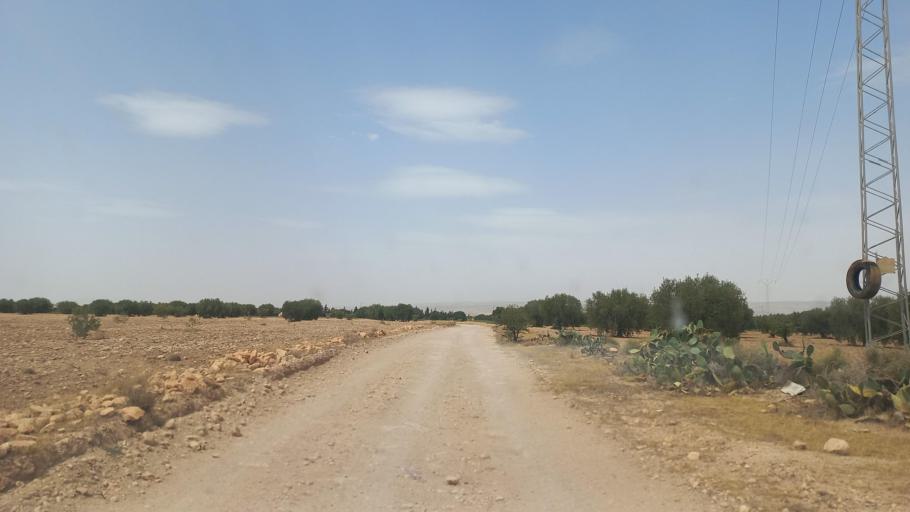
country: TN
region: Al Qasrayn
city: Kasserine
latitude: 35.2564
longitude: 9.0053
